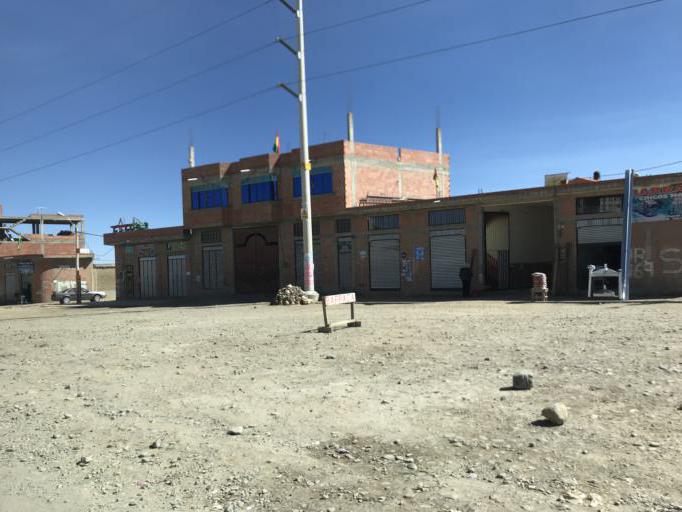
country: BO
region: La Paz
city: La Paz
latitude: -16.5007
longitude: -68.2381
